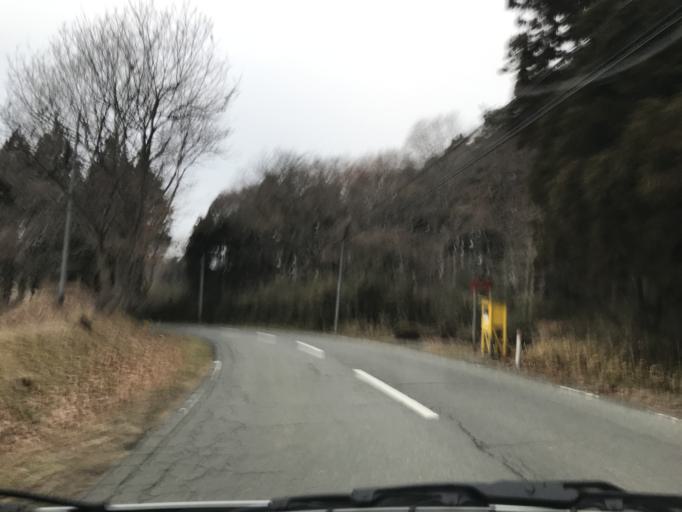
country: JP
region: Miyagi
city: Wakuya
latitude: 38.6773
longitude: 141.1021
